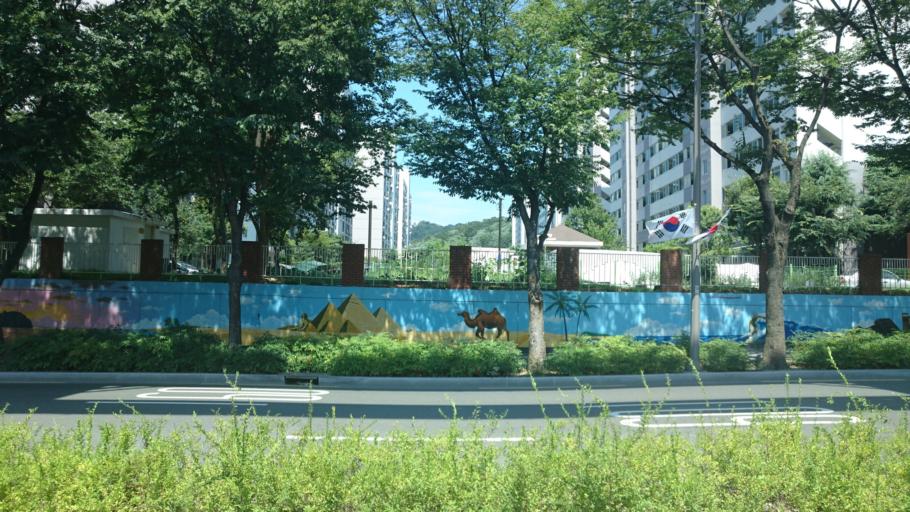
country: KR
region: Daegu
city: Daegu
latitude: 35.8185
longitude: 128.6440
